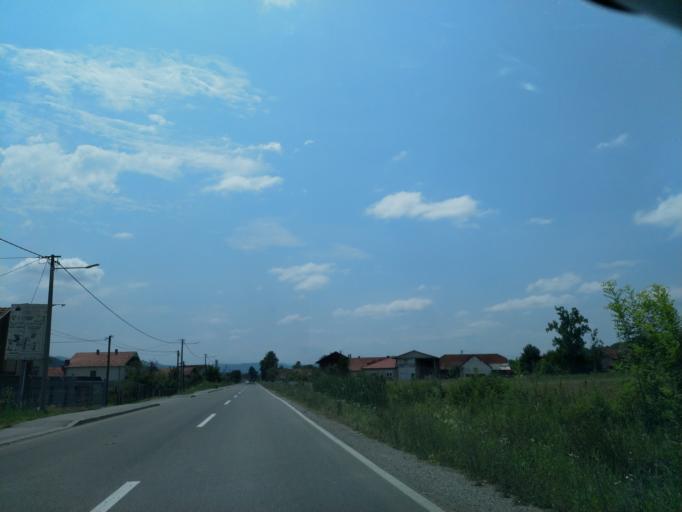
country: RS
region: Central Serbia
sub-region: Rasinski Okrug
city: Krusevac
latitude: 43.5080
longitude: 21.3012
